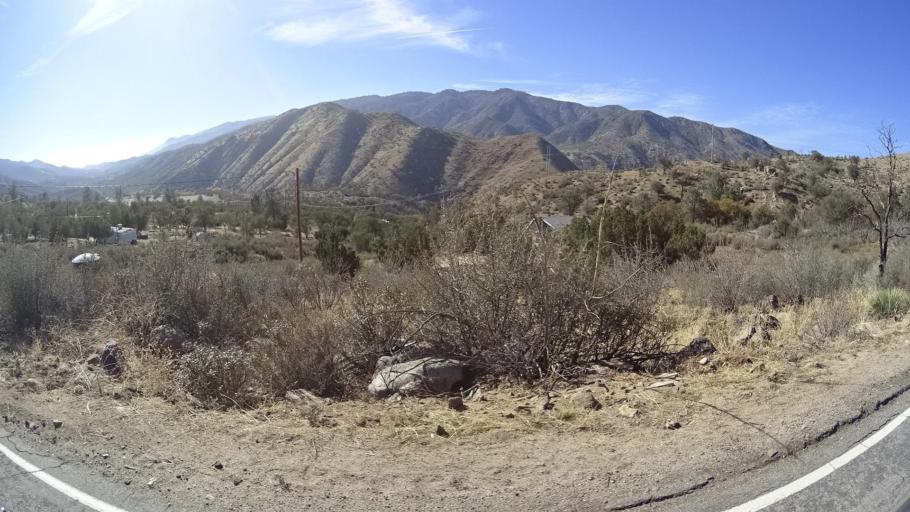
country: US
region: California
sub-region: Kern County
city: Bodfish
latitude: 35.5509
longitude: -118.5059
